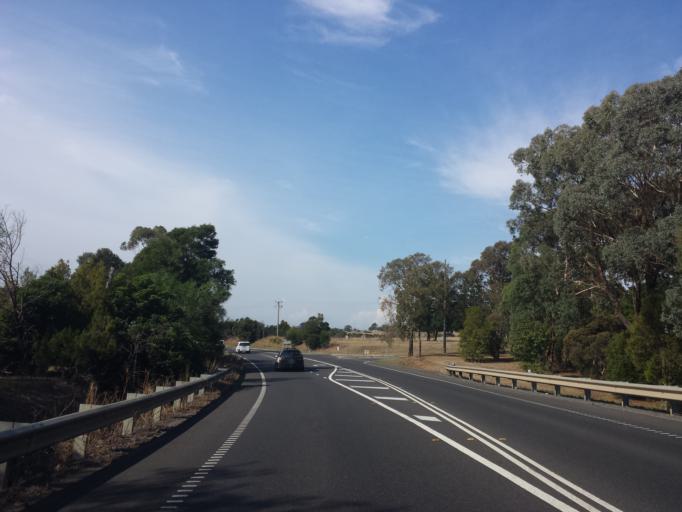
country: AU
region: Victoria
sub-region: Casey
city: Narre Warren North
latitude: -37.9773
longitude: 145.3140
